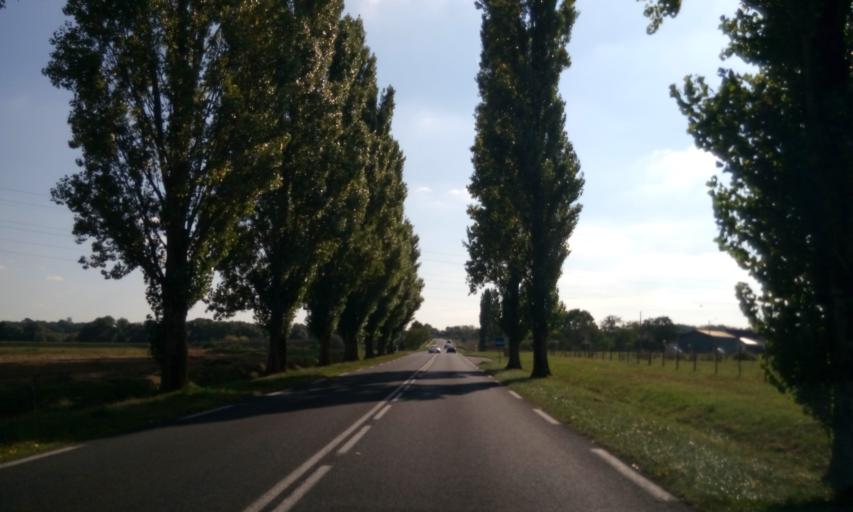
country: FR
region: Centre
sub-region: Departement d'Indre-et-Loire
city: Poce-sur-Cisse
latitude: 47.4370
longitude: 1.0067
